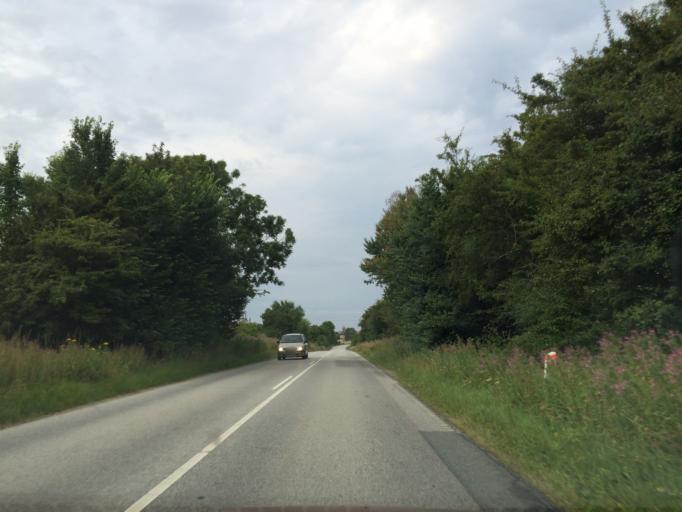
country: DK
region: South Denmark
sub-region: Sonderborg Kommune
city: Broager
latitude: 54.9054
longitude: 9.6757
